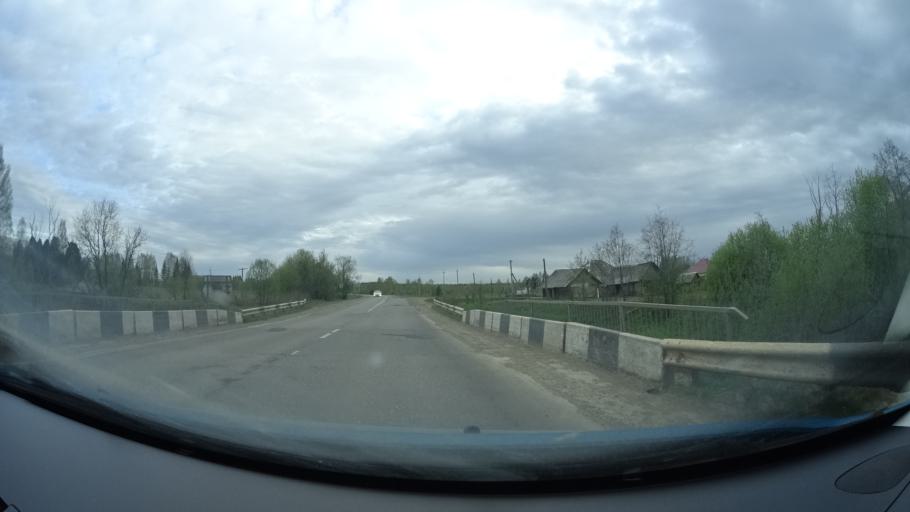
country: RU
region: Perm
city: Osa
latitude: 57.3682
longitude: 55.6063
